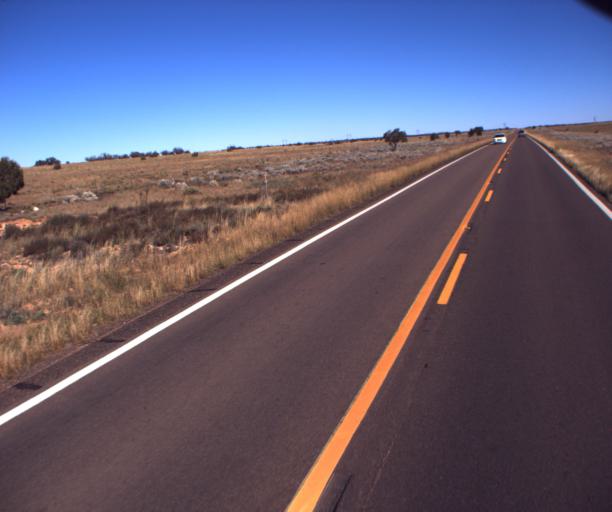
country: US
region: Arizona
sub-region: Navajo County
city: Snowflake
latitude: 34.5995
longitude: -110.0880
